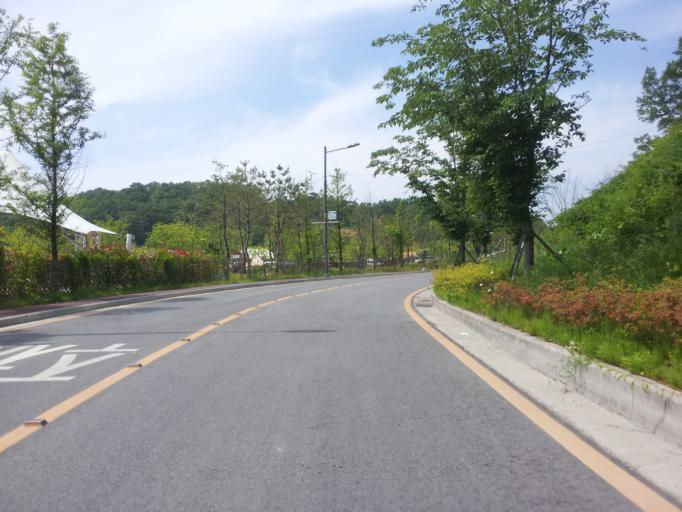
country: KR
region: Daejeon
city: Sintansin
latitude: 36.4557
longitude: 127.4755
